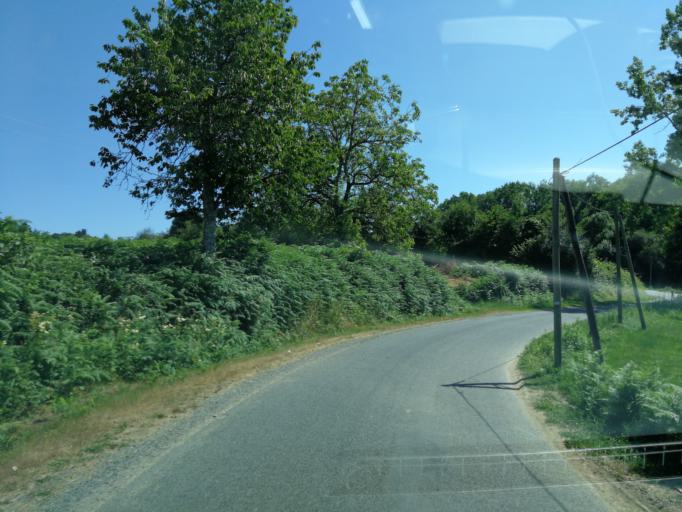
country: FR
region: Limousin
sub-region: Departement de la Correze
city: Sainte-Fereole
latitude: 45.2380
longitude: 1.5941
